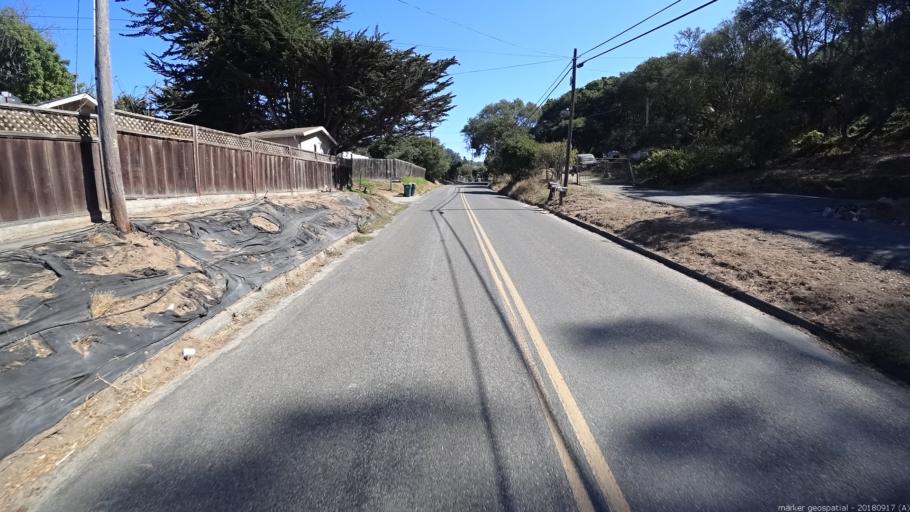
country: US
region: California
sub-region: Monterey County
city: Elkhorn
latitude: 36.8280
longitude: -121.7076
